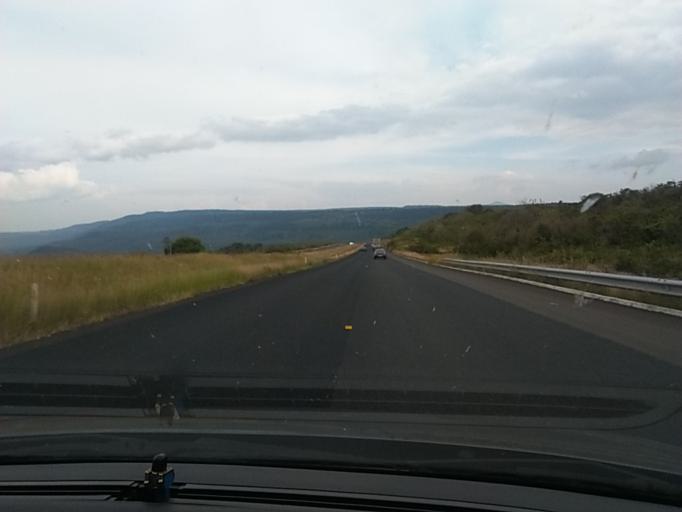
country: MX
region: Mexico
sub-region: Chapultepec
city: Chucandiro
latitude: 19.8802
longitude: -101.4073
